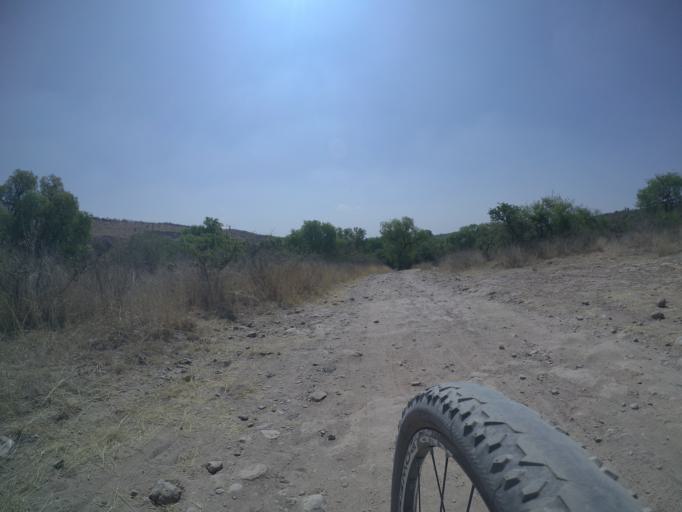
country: MX
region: Aguascalientes
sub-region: Jesus Maria
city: Paseos de las Haciendas [Fraccionamiento]
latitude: 22.0023
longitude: -102.3692
